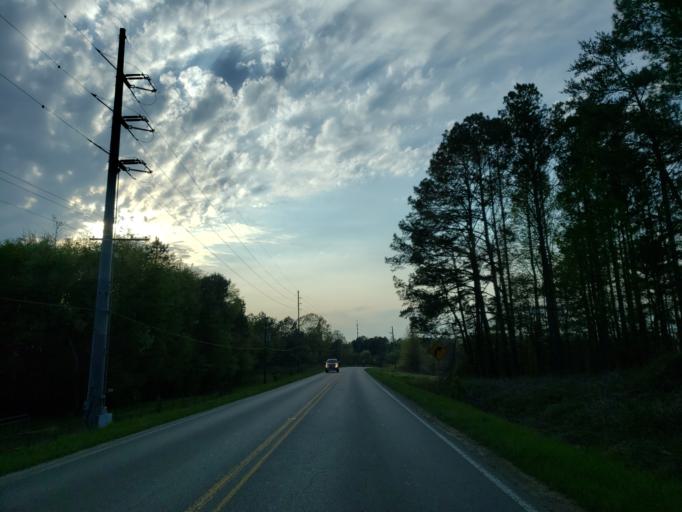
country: US
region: Georgia
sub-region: Cherokee County
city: Ball Ground
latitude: 34.3042
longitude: -84.4019
